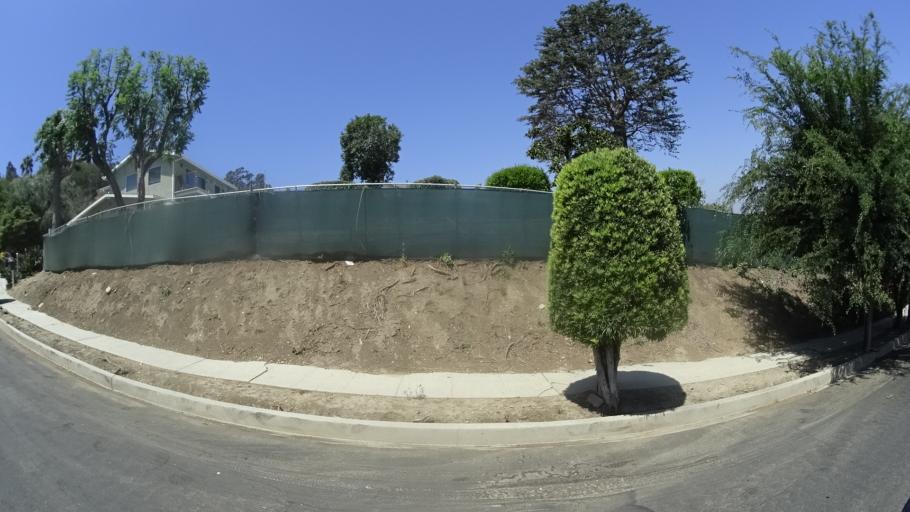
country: US
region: California
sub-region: Los Angeles County
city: Ladera Heights
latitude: 34.0166
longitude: -118.3671
